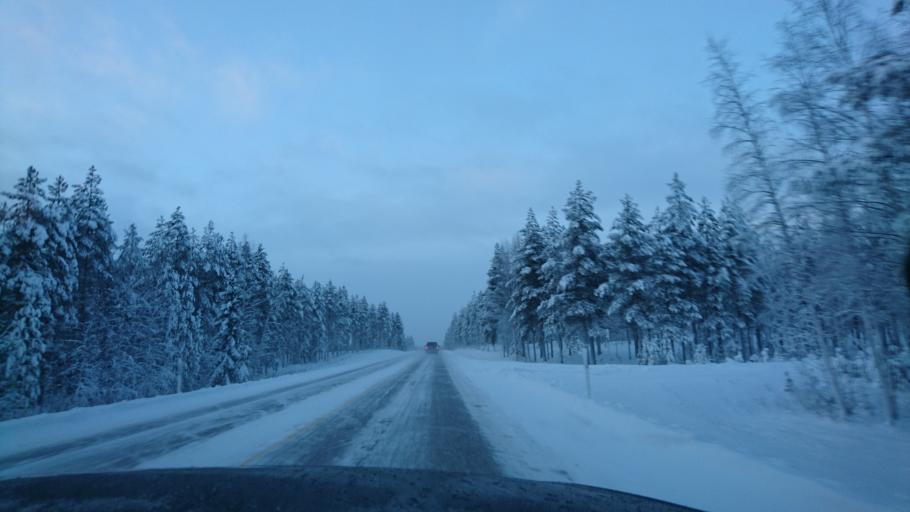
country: FI
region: Northern Ostrobothnia
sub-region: Koillismaa
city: Taivalkoski
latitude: 65.4679
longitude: 27.6756
